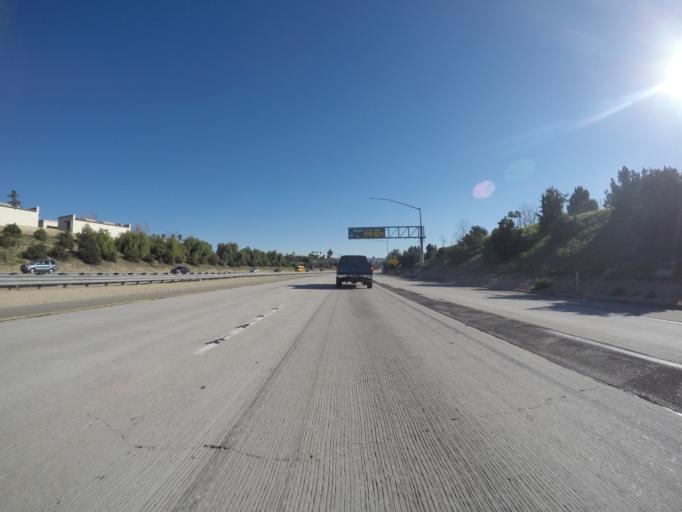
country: US
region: California
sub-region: San Bernardino County
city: Highland
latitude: 34.1269
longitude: -117.2020
